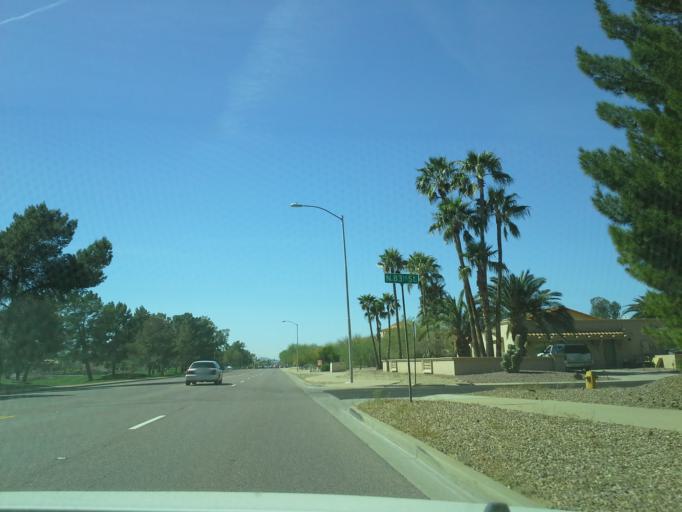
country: US
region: Arizona
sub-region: Maricopa County
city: Paradise Valley
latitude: 33.5966
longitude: -111.9026
